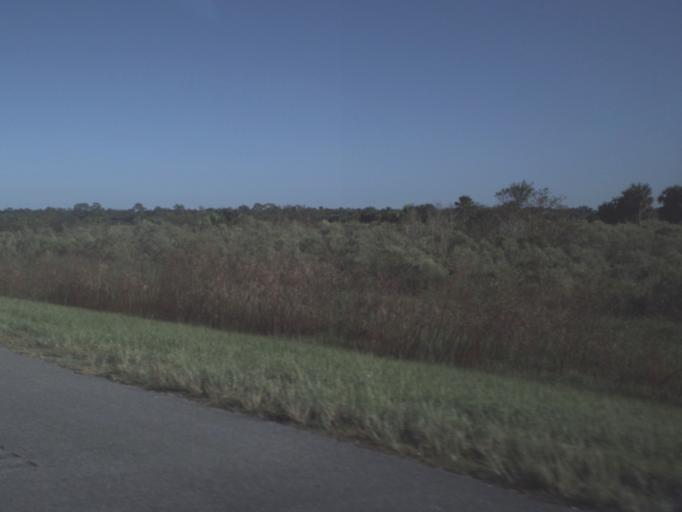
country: US
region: Florida
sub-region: Seminole County
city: Midway
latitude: 28.7290
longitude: -81.2486
